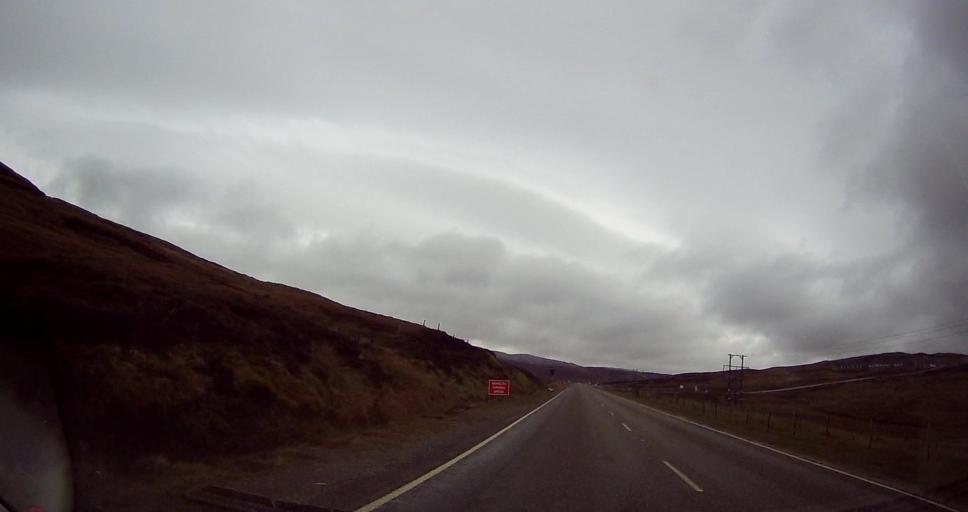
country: GB
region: Scotland
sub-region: Shetland Islands
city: Lerwick
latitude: 60.2706
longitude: -1.2359
